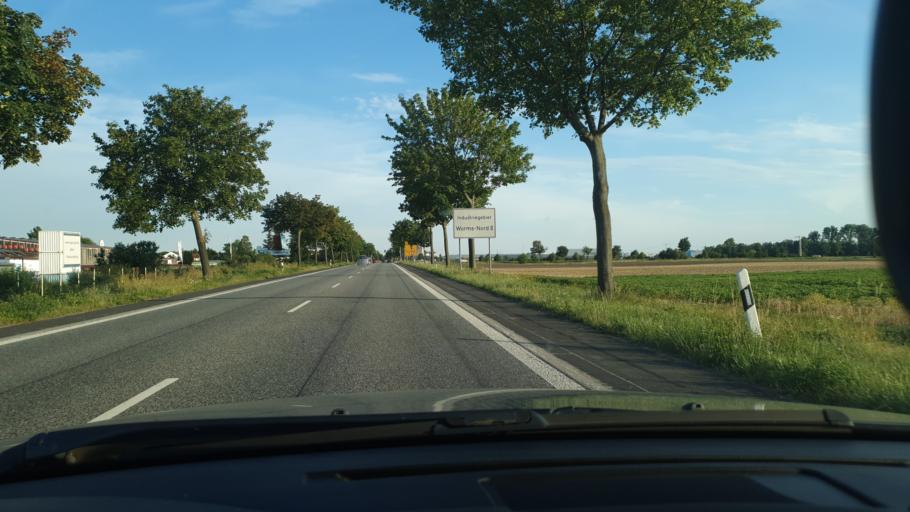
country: DE
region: Rheinland-Pfalz
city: Osthofen
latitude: 49.7092
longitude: 8.3490
